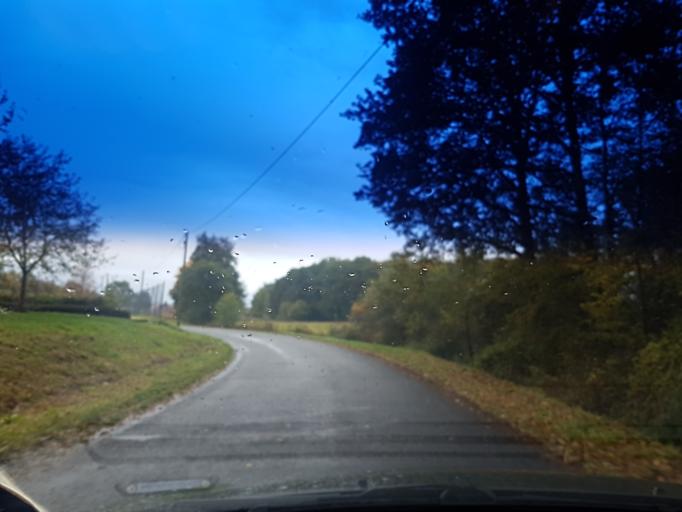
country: DE
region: Bavaria
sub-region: Regierungsbezirk Mittelfranken
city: Wachenroth
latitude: 49.7545
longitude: 10.7009
